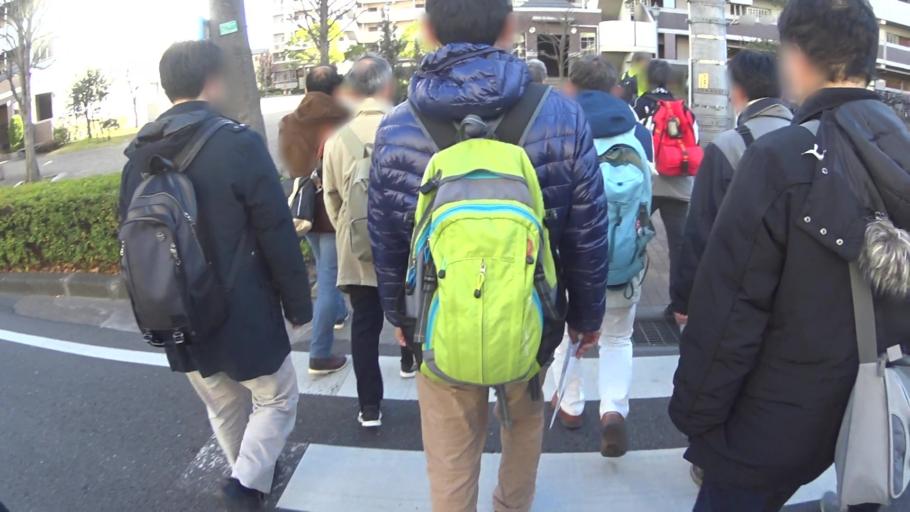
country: JP
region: Saitama
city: Shimotoda
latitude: 35.8443
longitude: 139.6760
